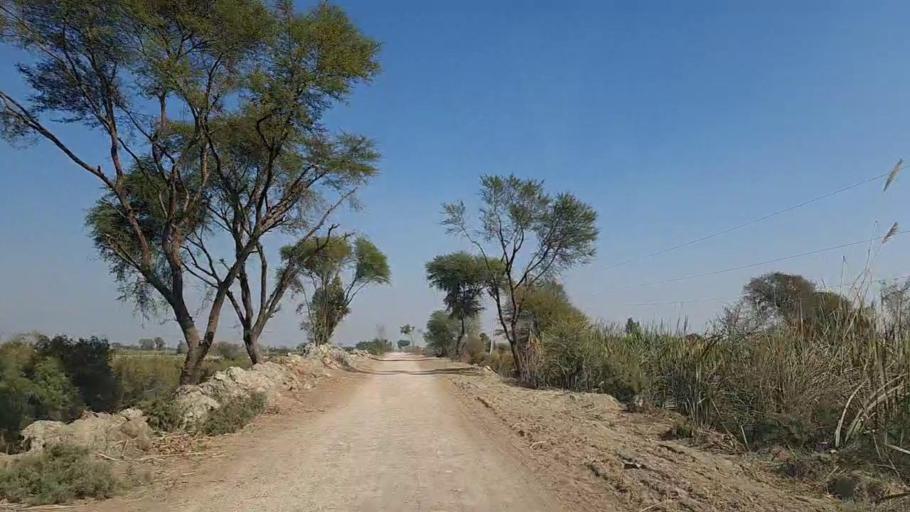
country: PK
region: Sindh
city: Bandhi
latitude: 26.5429
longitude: 68.3257
